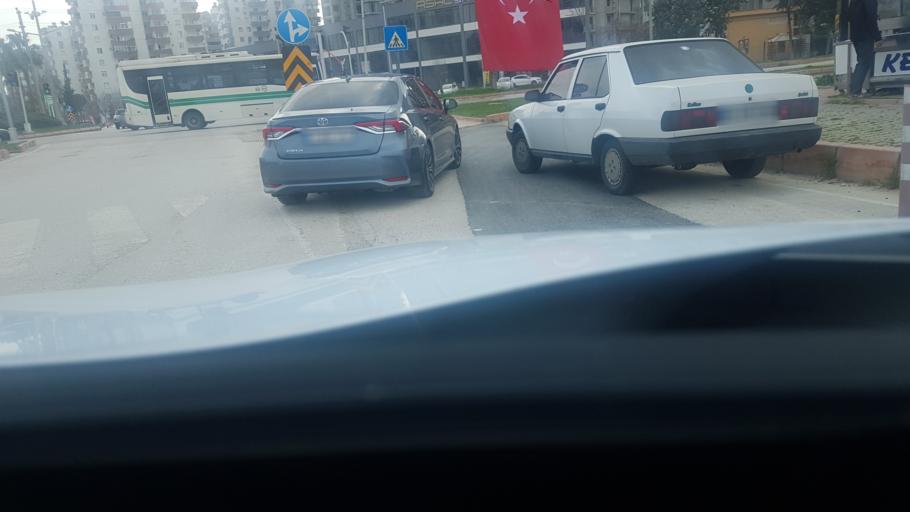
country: TR
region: Adana
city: Seyhan
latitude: 37.0531
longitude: 35.2531
